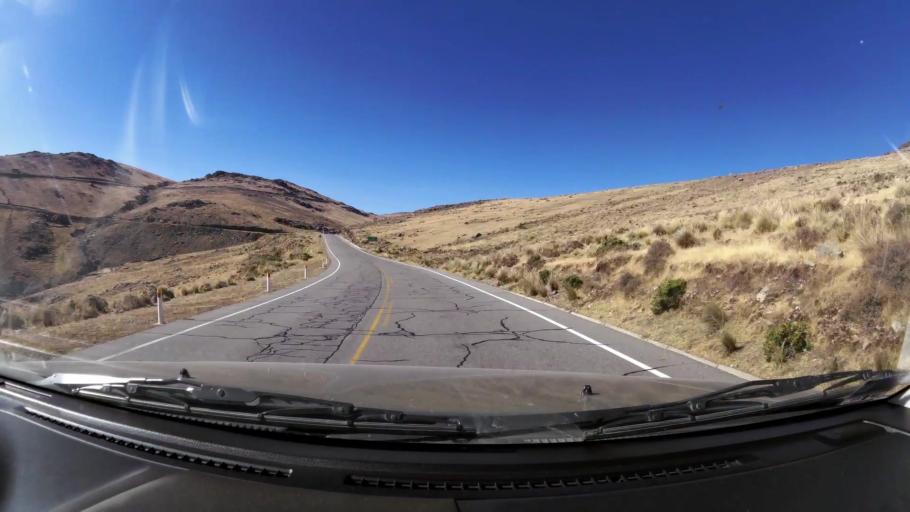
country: PE
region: Huancavelica
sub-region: Huaytara
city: Huayacundo Arma
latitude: -13.5682
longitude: -75.2352
